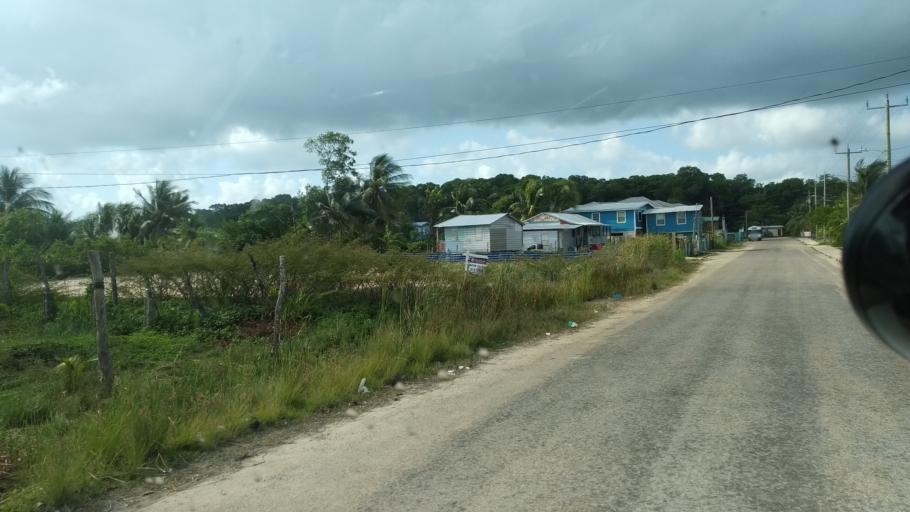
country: BZ
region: Belize
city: Belize City
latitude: 17.5155
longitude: -88.2327
